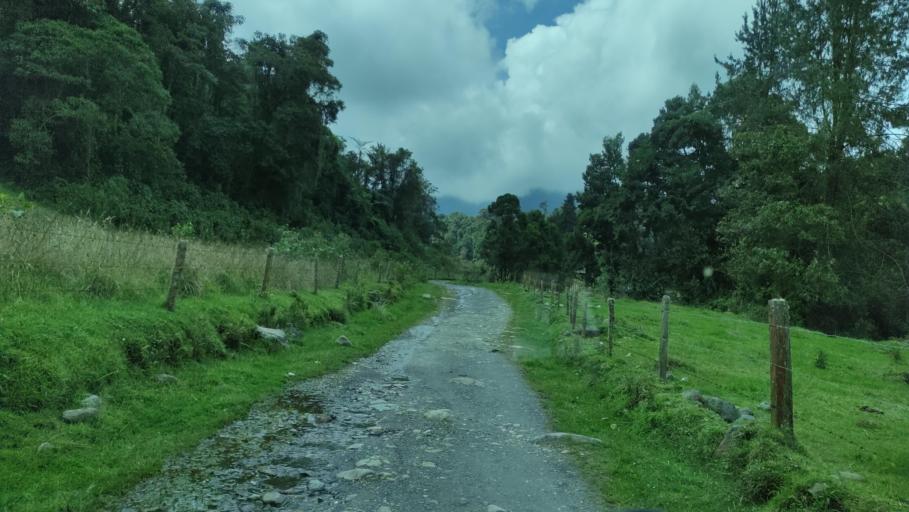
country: CO
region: Caldas
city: Villamaria
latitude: 4.9852
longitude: -75.4420
